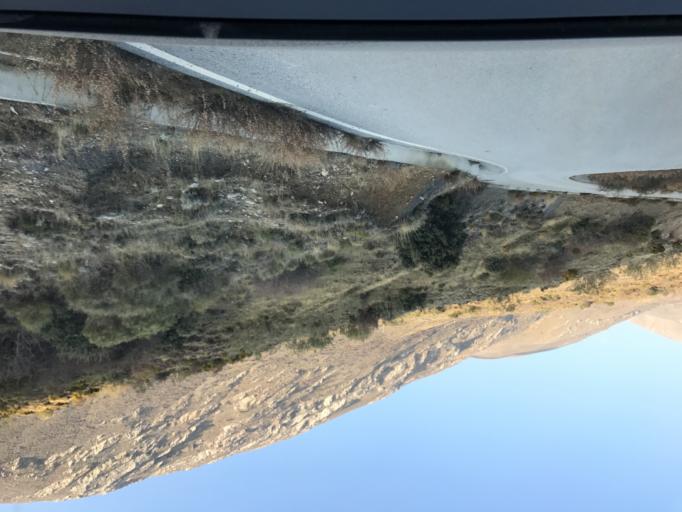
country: ES
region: Andalusia
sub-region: Provincia de Granada
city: Guejar-Sierra
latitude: 37.1796
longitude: -3.4314
